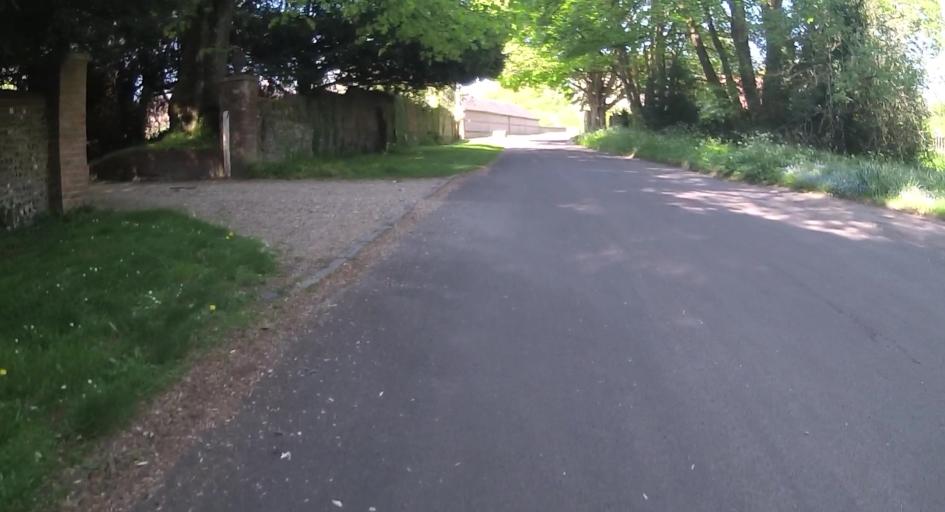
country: GB
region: England
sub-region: Hampshire
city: Alton
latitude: 51.1718
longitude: -1.0073
